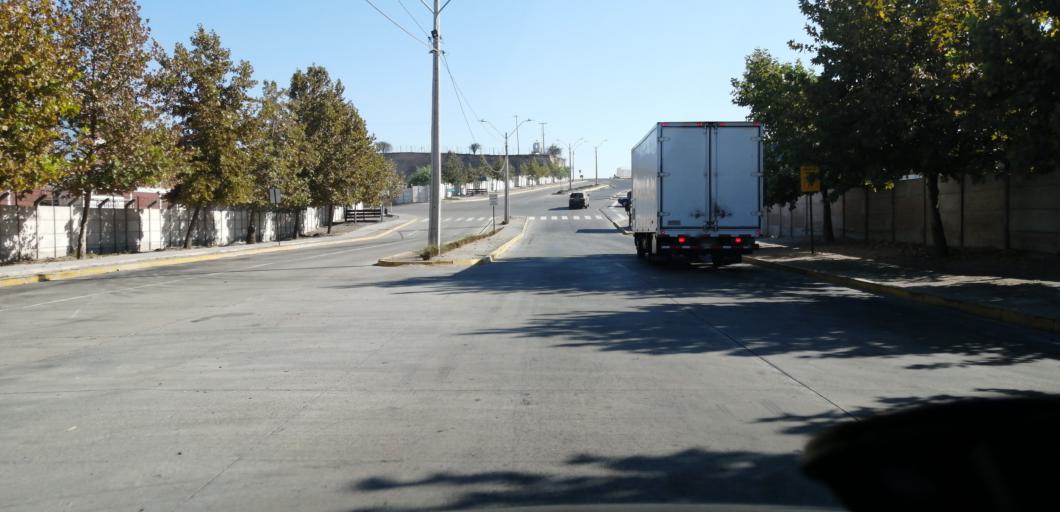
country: CL
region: Santiago Metropolitan
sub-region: Provincia de Santiago
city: Lo Prado
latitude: -33.4549
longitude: -70.7980
